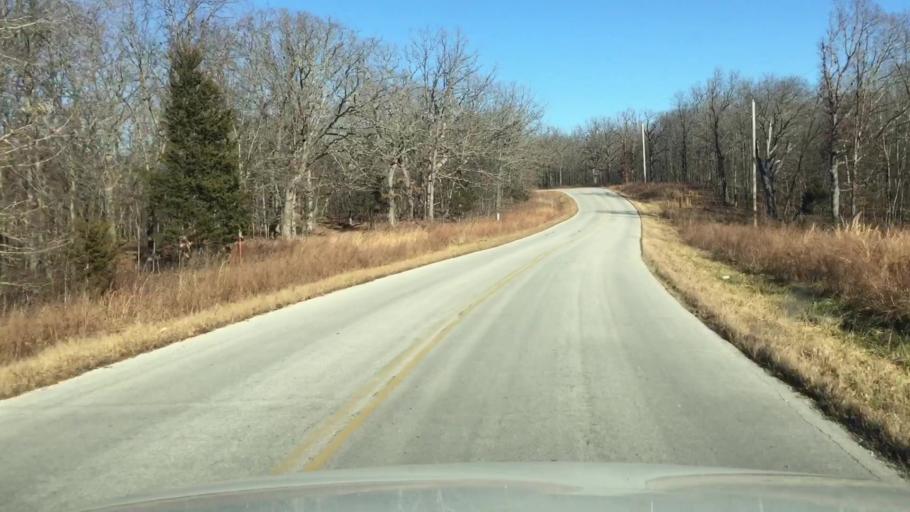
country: US
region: Missouri
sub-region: Morgan County
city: Versailles
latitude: 38.3317
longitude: -92.7712
